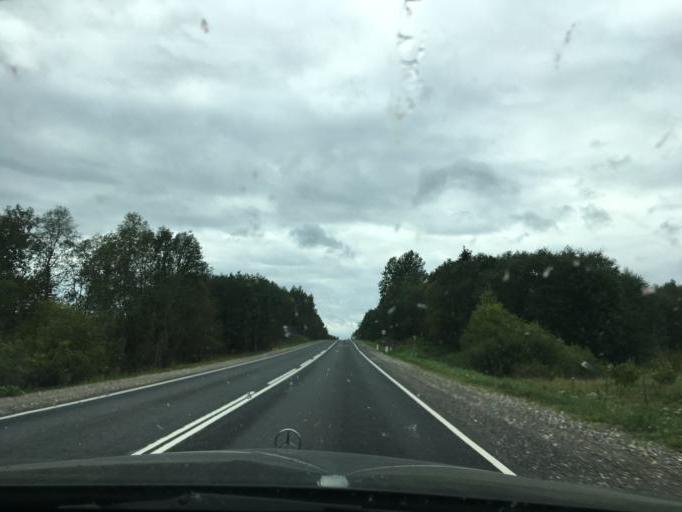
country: RU
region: Pskov
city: Pechory
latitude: 57.6576
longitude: 27.4576
